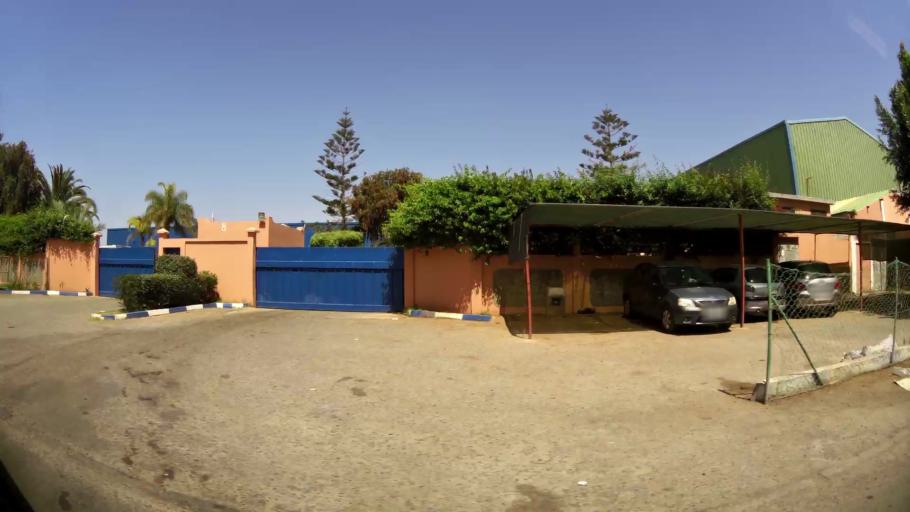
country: MA
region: Souss-Massa-Draa
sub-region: Inezgane-Ait Mellou
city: Inezgane
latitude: 30.3261
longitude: -9.4894
